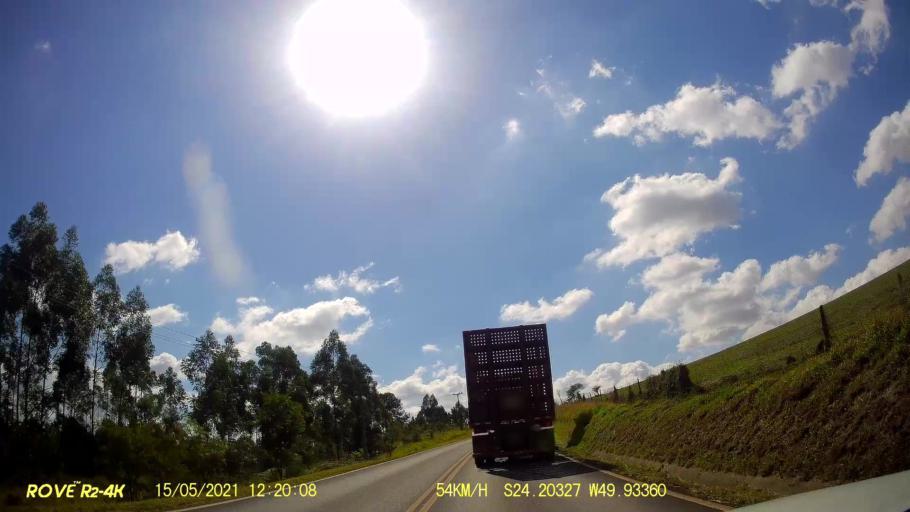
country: BR
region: Parana
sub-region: Jaguariaiva
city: Jaguariaiva
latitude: -24.2033
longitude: -49.9337
